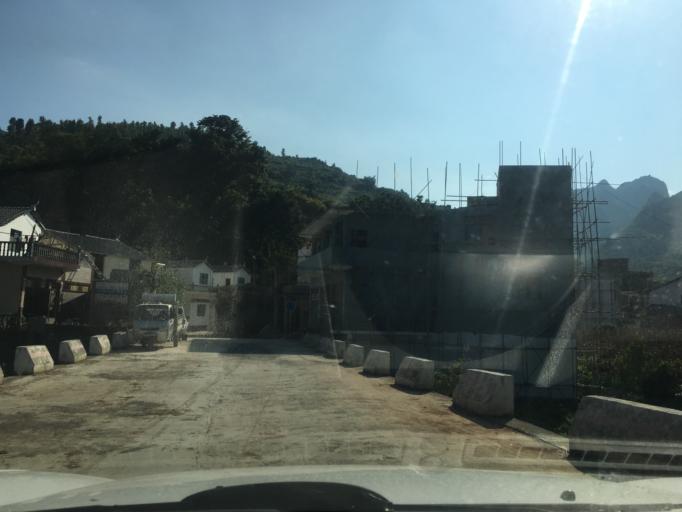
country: CN
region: Guangxi Zhuangzu Zizhiqu
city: Xinzhou
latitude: 25.4442
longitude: 105.7366
